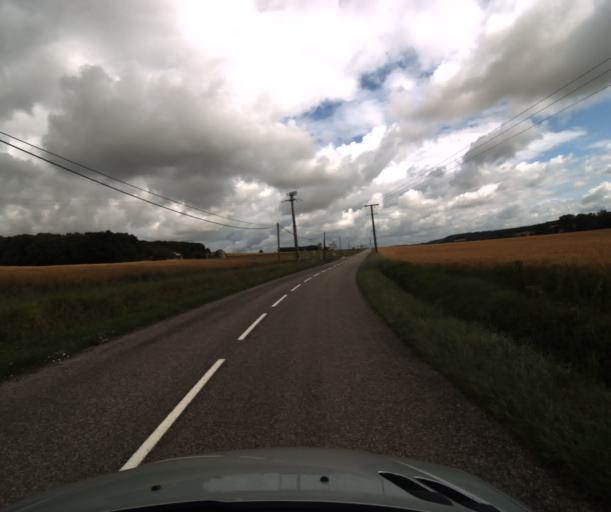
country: FR
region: Midi-Pyrenees
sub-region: Departement du Tarn-et-Garonne
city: Lavit
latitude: 43.9706
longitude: 0.9079
